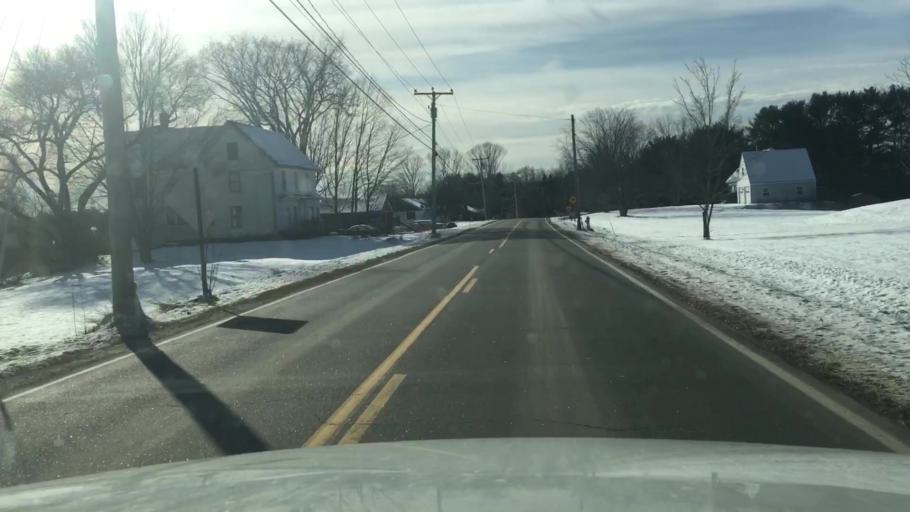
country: US
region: Maine
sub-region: Lincoln County
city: Wiscasset
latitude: 43.9656
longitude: -69.6984
